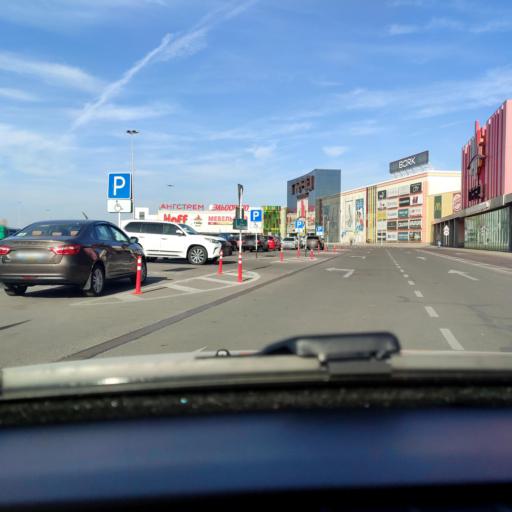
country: RU
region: Voronezj
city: Podgornoye
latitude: 51.7881
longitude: 39.2036
